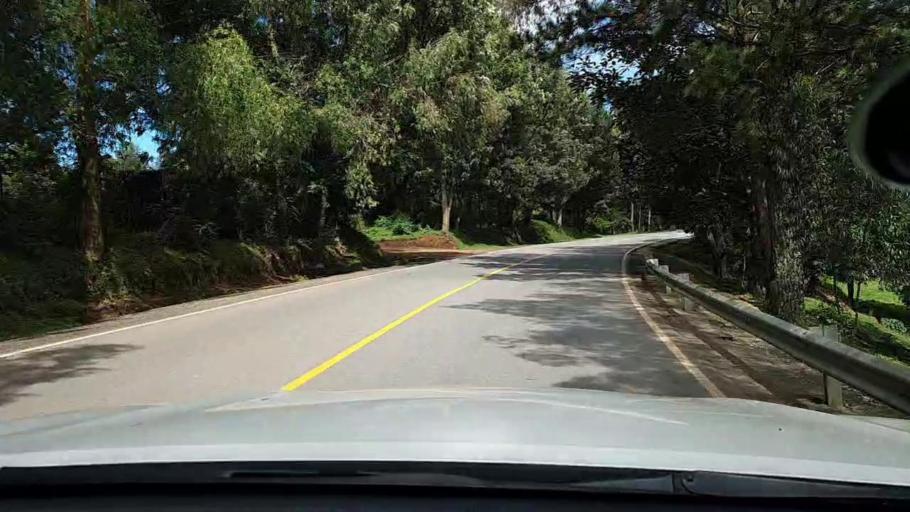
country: RW
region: Kigali
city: Kigali
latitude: -1.8230
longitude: 29.9422
